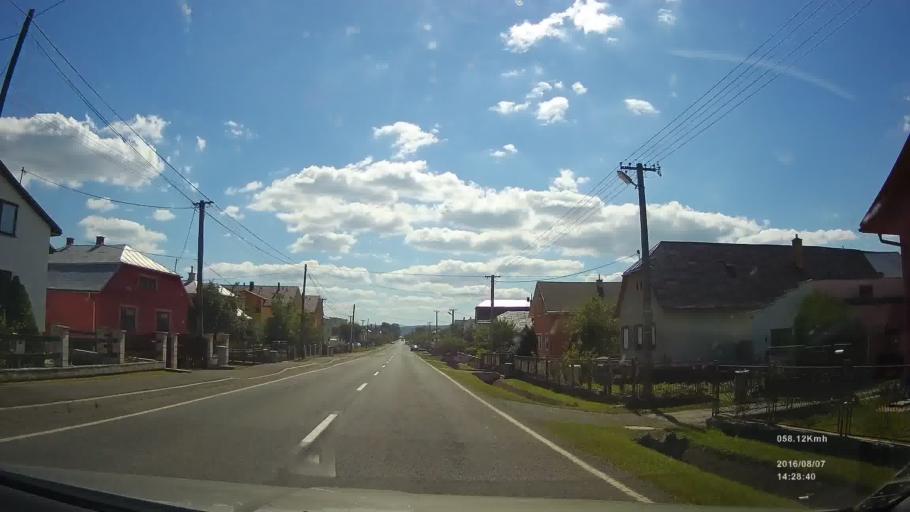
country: SK
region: Presovsky
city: Stropkov
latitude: 49.2479
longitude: 21.6840
